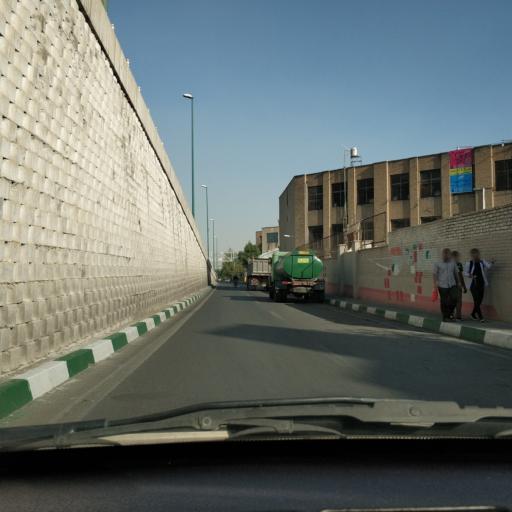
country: IR
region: Tehran
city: Tehran
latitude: 35.7217
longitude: 51.4744
